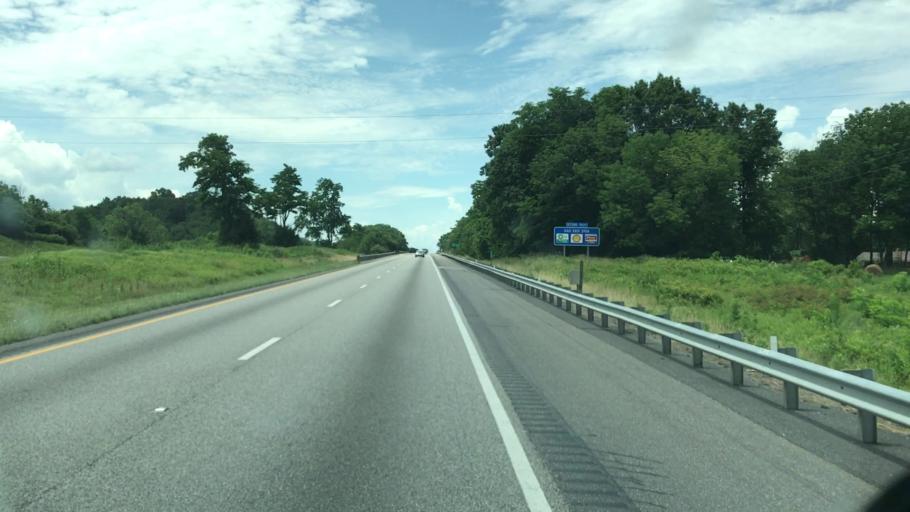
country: US
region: Virginia
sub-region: Augusta County
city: Jolivue
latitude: 38.0438
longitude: -79.1229
